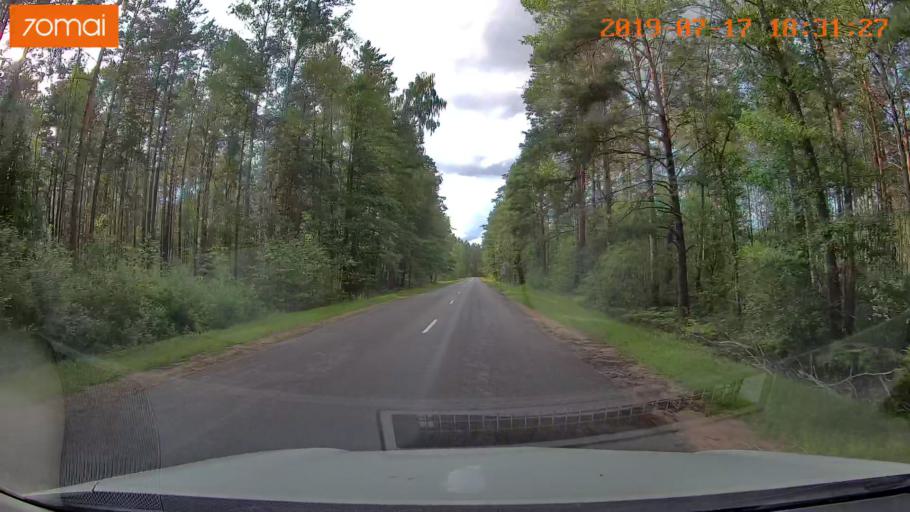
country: BY
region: Mogilev
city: Asipovichy
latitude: 53.2593
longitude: 28.6821
